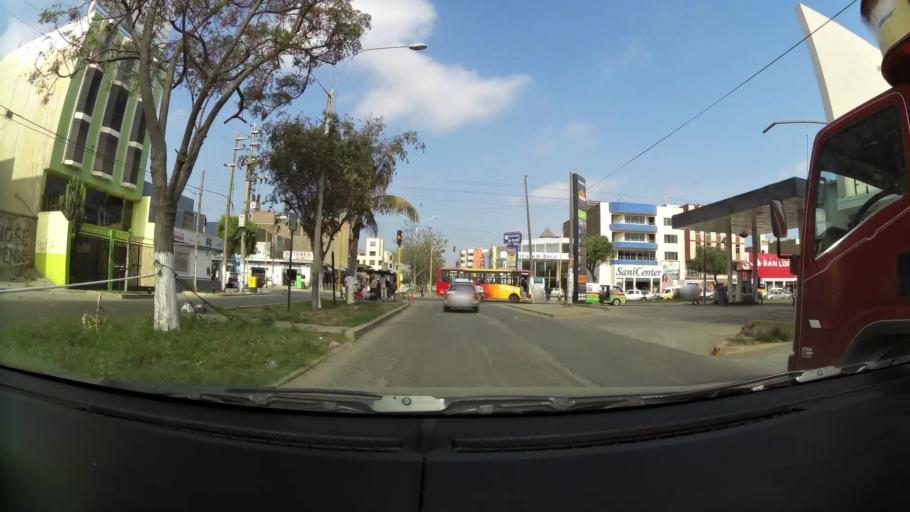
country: PE
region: La Libertad
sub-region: Provincia de Trujillo
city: Trujillo
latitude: -8.1125
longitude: -79.0144
